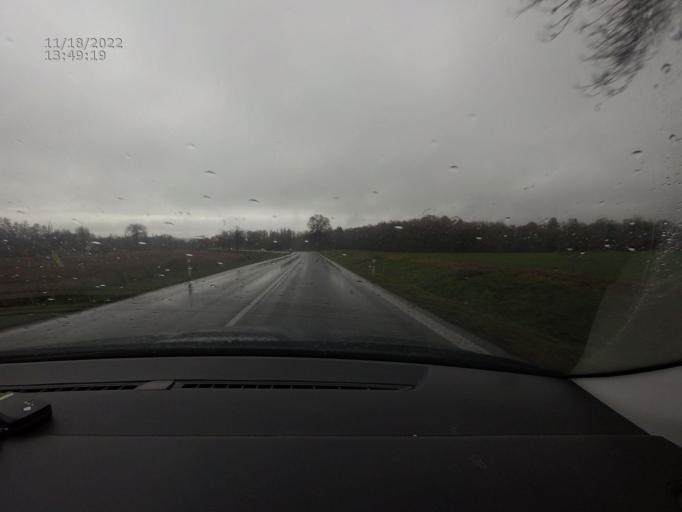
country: CZ
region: Jihocesky
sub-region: Okres Strakonice
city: Blatna
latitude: 49.4140
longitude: 13.8952
